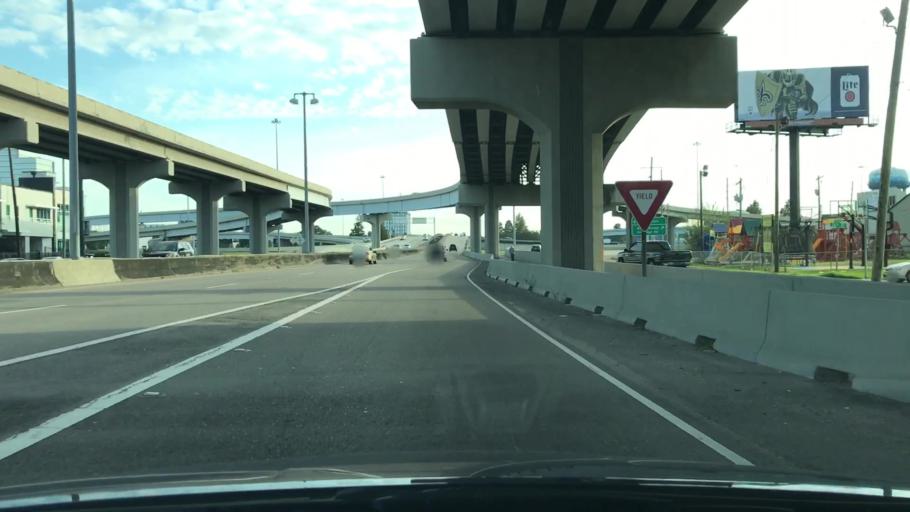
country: US
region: Louisiana
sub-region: Jefferson Parish
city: Metairie
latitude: 30.0017
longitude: -90.1555
